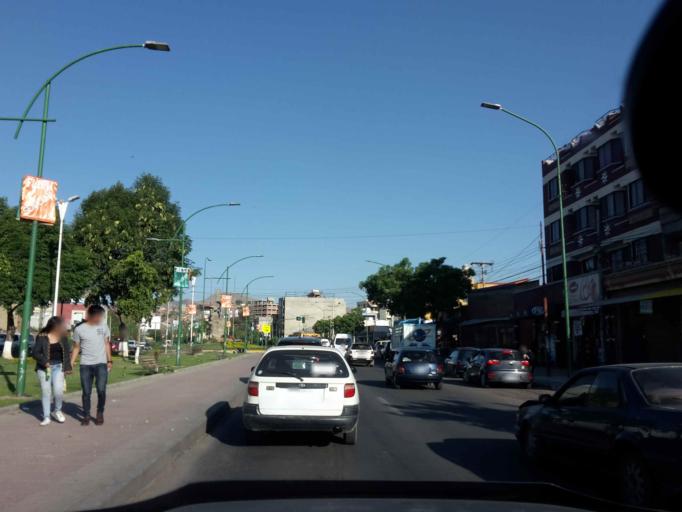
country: BO
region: Cochabamba
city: Cochabamba
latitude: -17.4126
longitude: -66.1605
